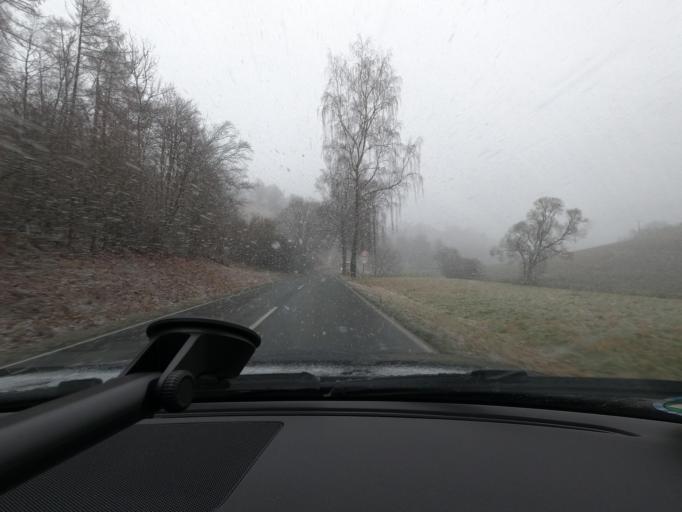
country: DE
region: North Rhine-Westphalia
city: Marsberg
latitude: 51.5059
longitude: 8.9007
